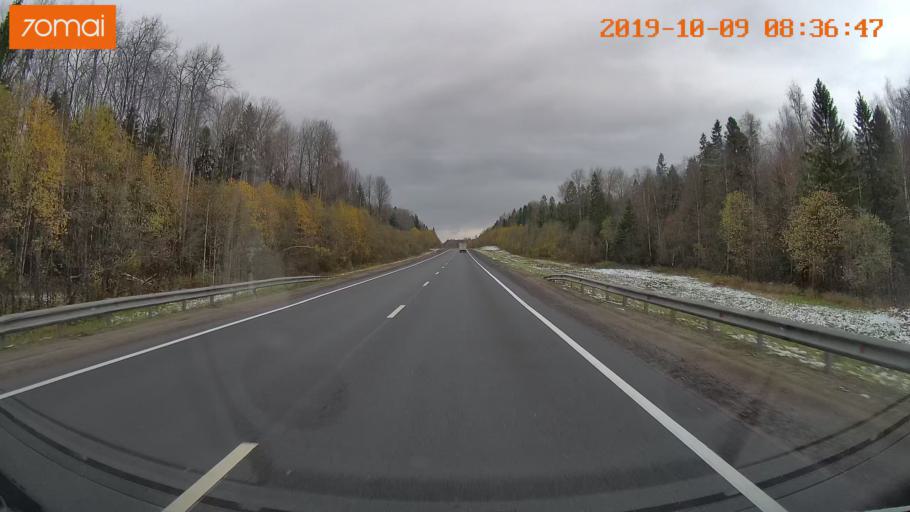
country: RU
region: Vologda
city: Gryazovets
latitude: 58.9315
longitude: 40.1759
